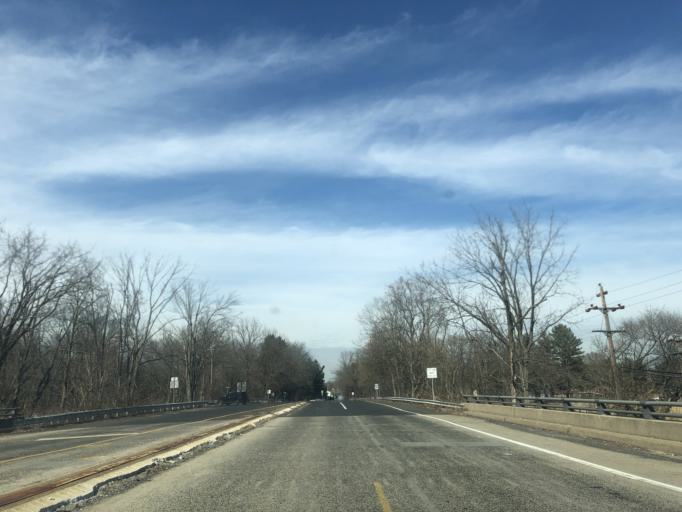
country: US
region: Pennsylvania
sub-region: Bucks County
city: Langhorne Manor
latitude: 40.1710
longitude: -74.9147
